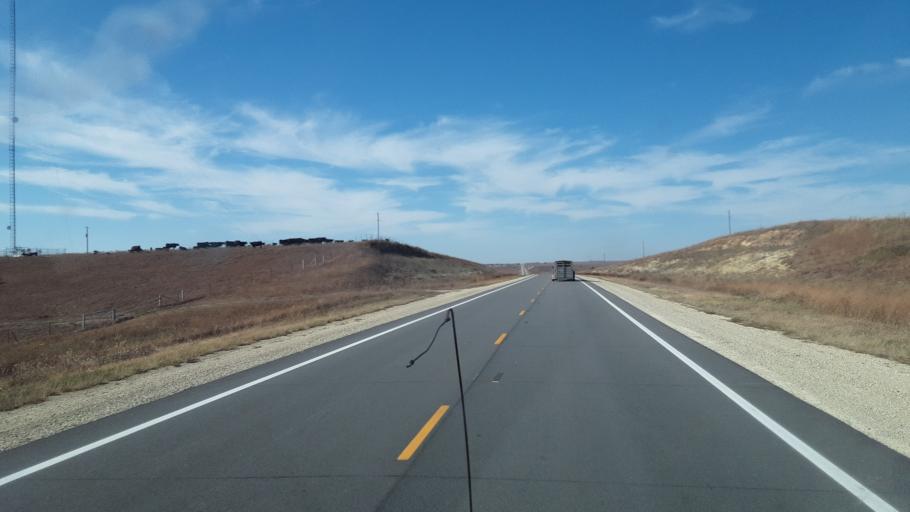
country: US
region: Kansas
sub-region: Chase County
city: Cottonwood Falls
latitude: 38.3625
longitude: -96.7357
